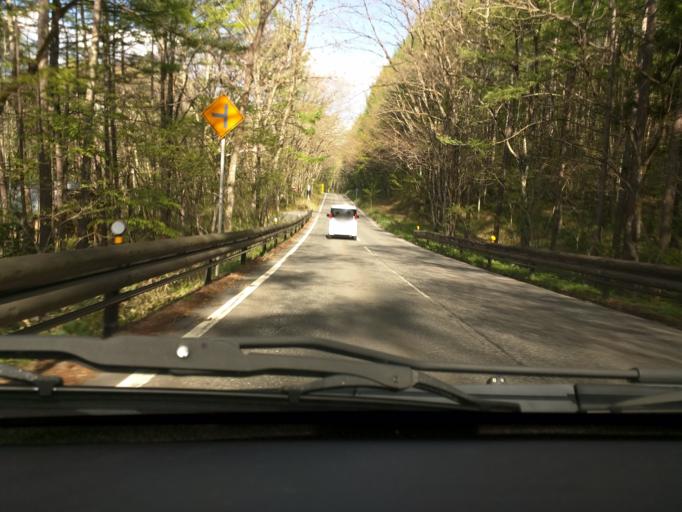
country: JP
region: Nagano
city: Nagano-shi
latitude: 36.7155
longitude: 138.1116
